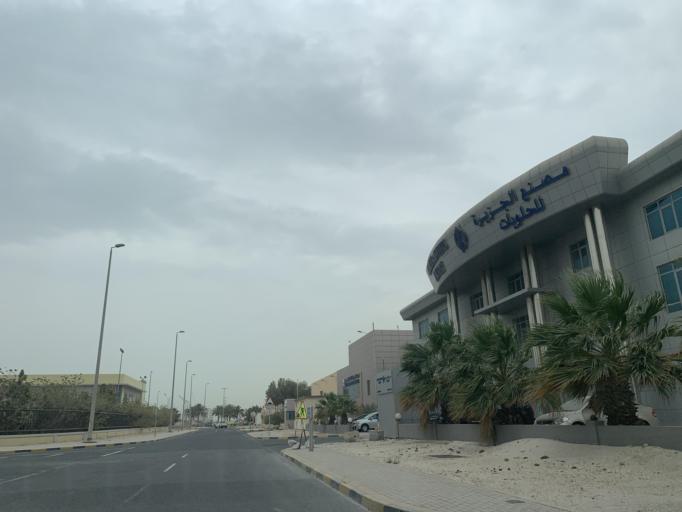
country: BH
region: Muharraq
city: Al Hadd
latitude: 26.2234
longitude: 50.6673
